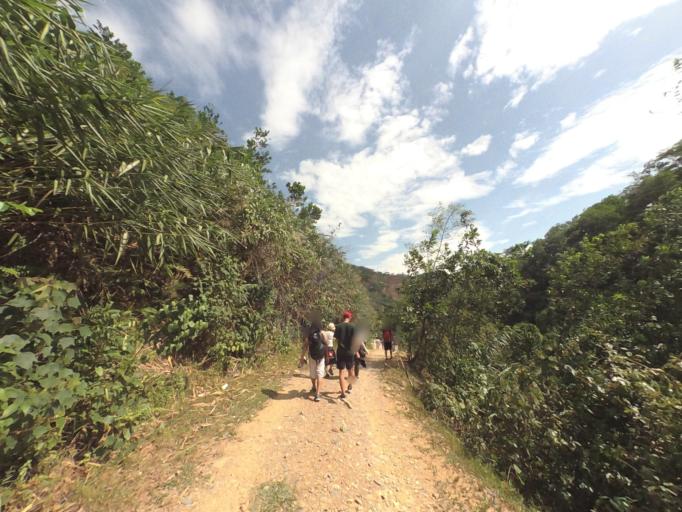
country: VN
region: Thua Thien-Hue
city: A Luoi
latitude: 16.3034
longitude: 107.3250
